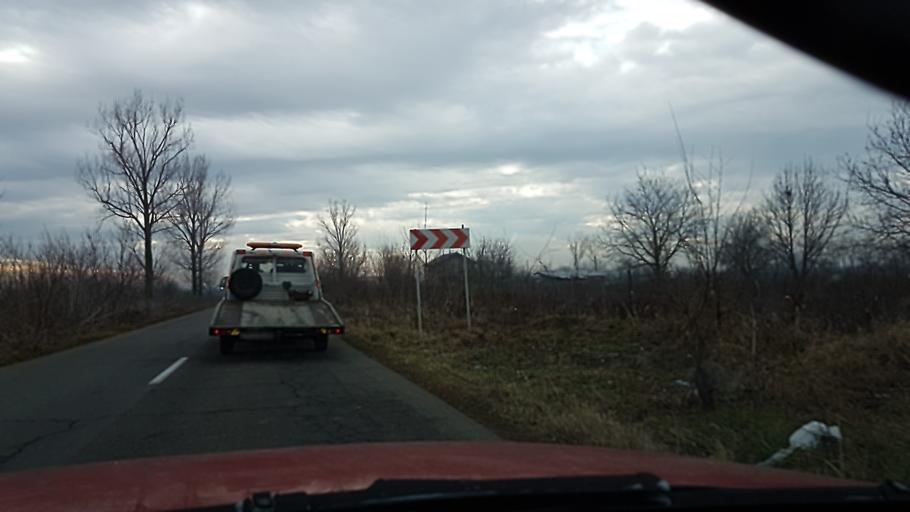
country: RO
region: Giurgiu
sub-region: Comuna Herasti
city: Herasti
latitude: 44.2215
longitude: 26.3613
